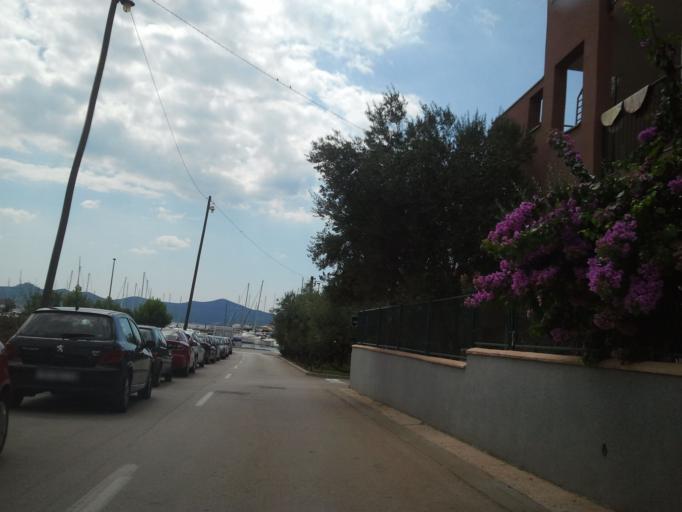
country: HR
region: Zadarska
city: Zadar
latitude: 44.1281
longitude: 15.2178
